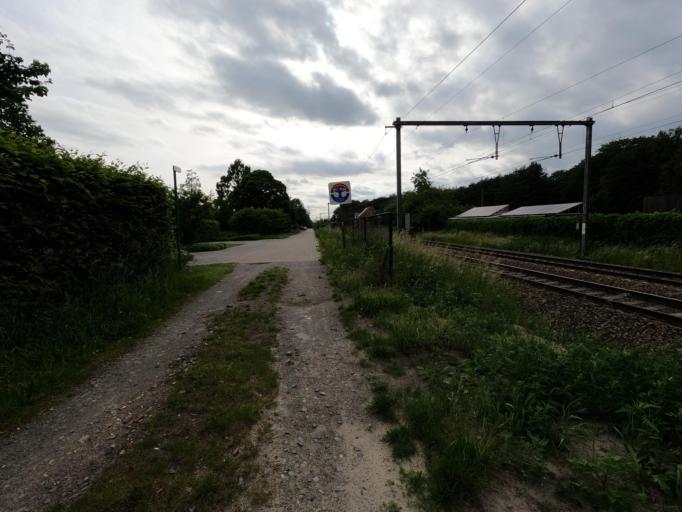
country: BE
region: Flanders
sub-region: Provincie Antwerpen
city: Herenthout
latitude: 51.1667
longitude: 4.7606
